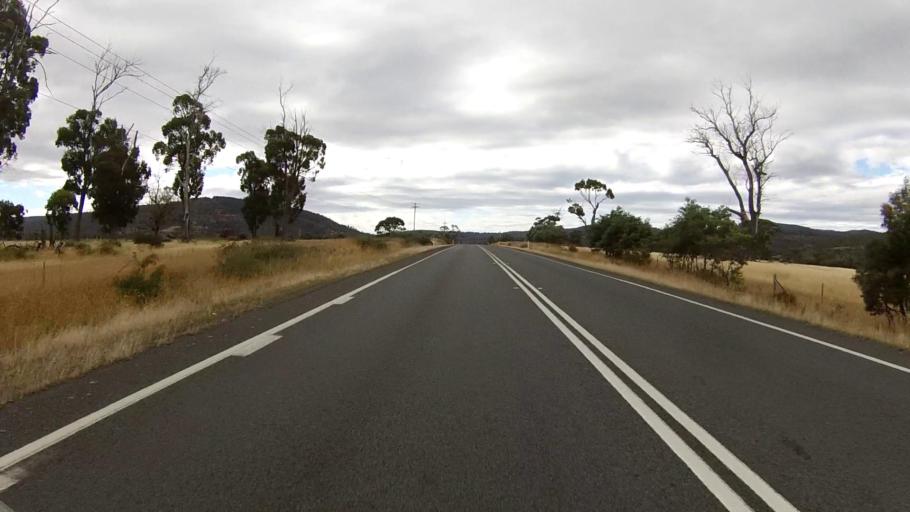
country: AU
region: Tasmania
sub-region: Sorell
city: Sorell
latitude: -42.5962
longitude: 147.7707
